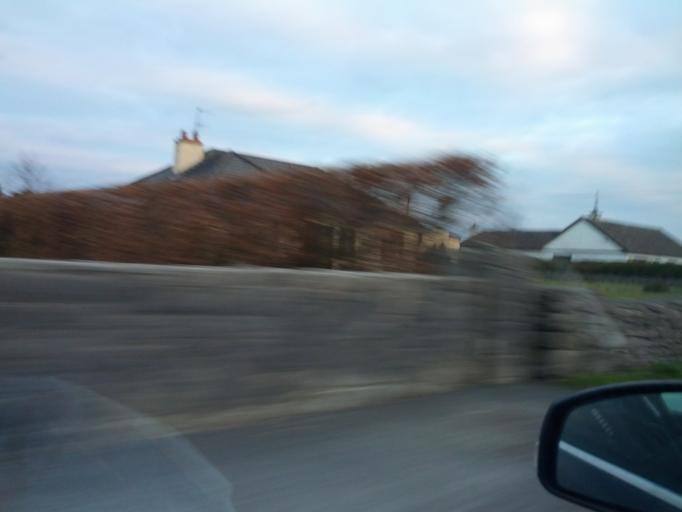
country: IE
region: Connaught
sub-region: County Galway
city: Athenry
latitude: 53.3257
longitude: -8.7647
